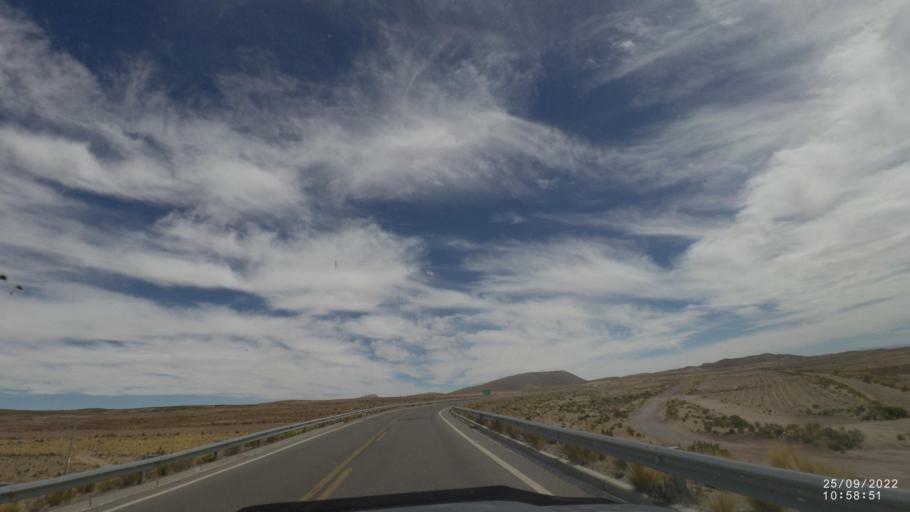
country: BO
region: Oruro
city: Challapata
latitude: -19.4579
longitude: -66.9088
